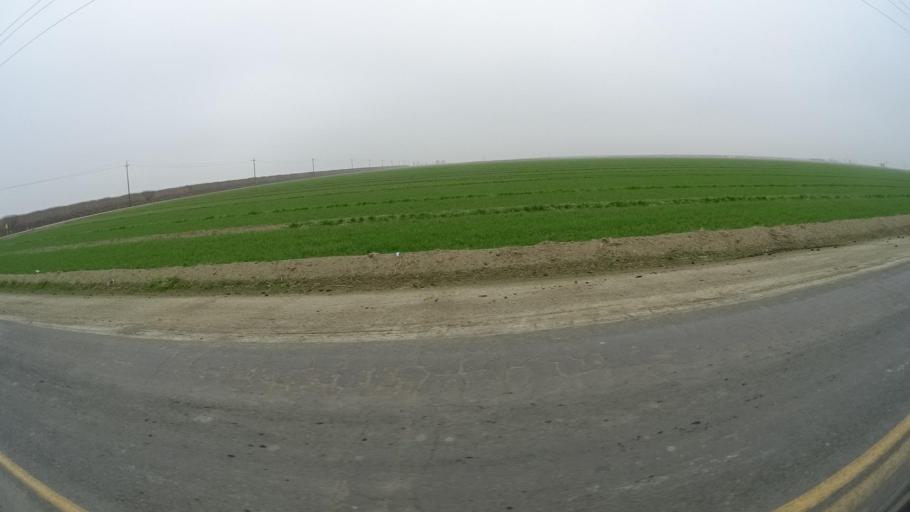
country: US
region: California
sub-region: Kern County
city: Wasco
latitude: 35.7175
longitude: -119.4363
